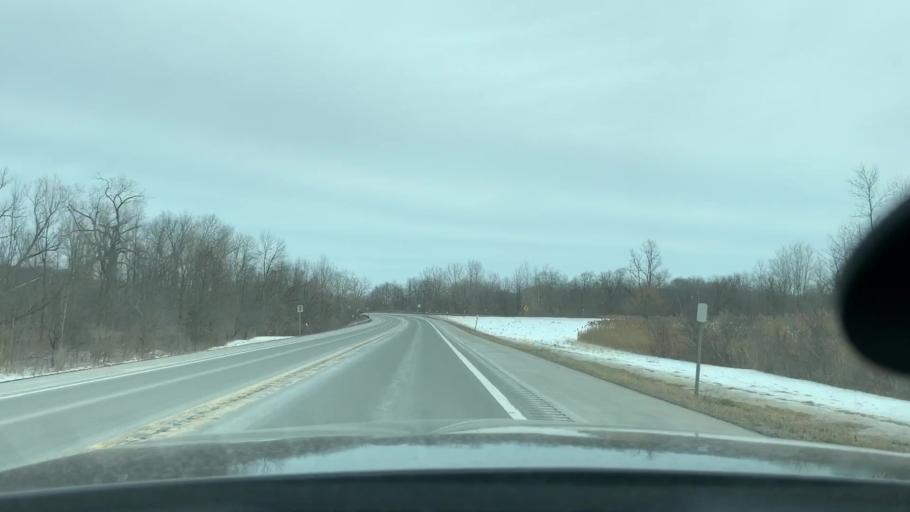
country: US
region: New York
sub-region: Herkimer County
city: Ilion
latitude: 43.0223
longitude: -75.0474
